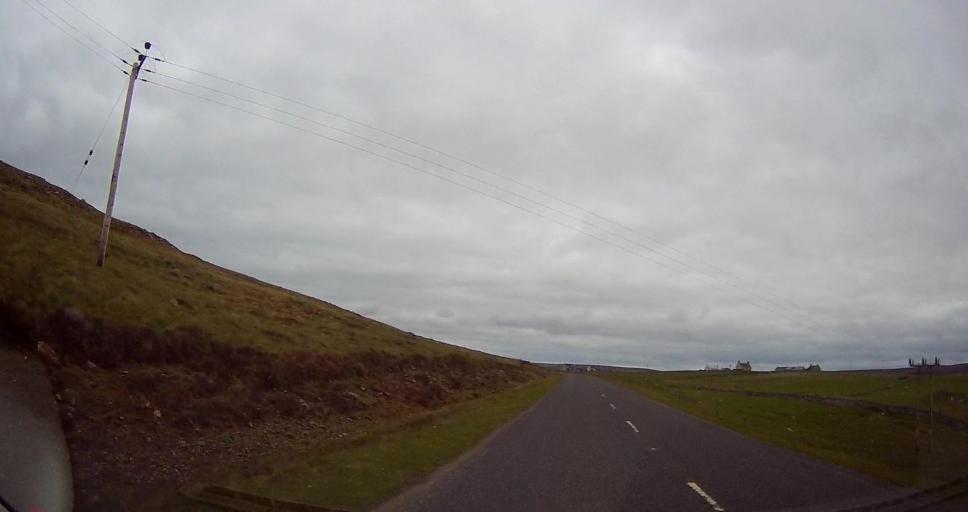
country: GB
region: Scotland
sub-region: Shetland Islands
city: Shetland
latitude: 60.6908
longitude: -0.9582
